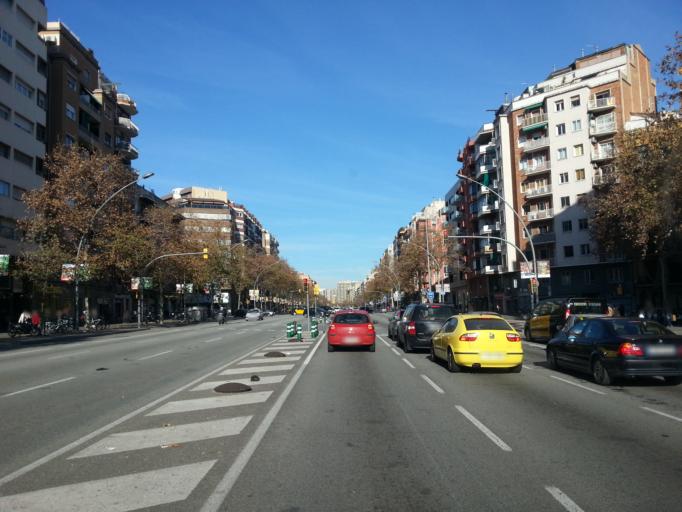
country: ES
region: Catalonia
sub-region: Provincia de Barcelona
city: Sant Marti
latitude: 41.4145
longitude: 2.1870
